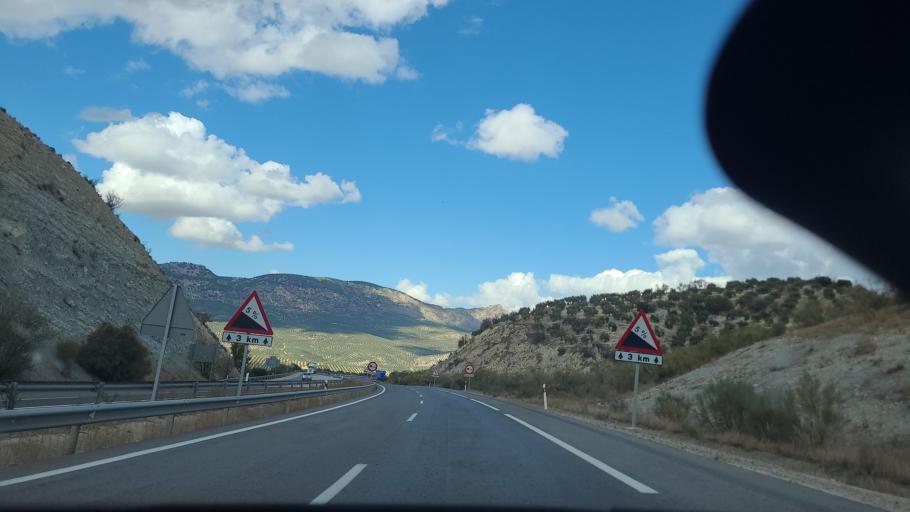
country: ES
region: Andalusia
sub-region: Provincia de Jaen
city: Campillo de Arenas
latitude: 37.5421
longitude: -3.6348
